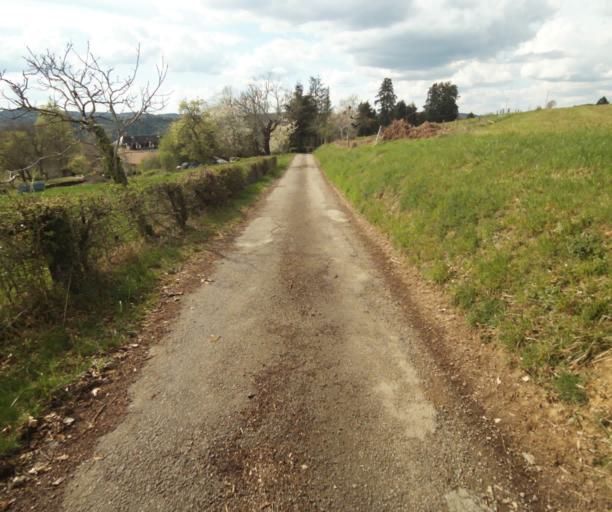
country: FR
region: Limousin
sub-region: Departement de la Correze
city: Tulle
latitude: 45.2824
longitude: 1.7455
